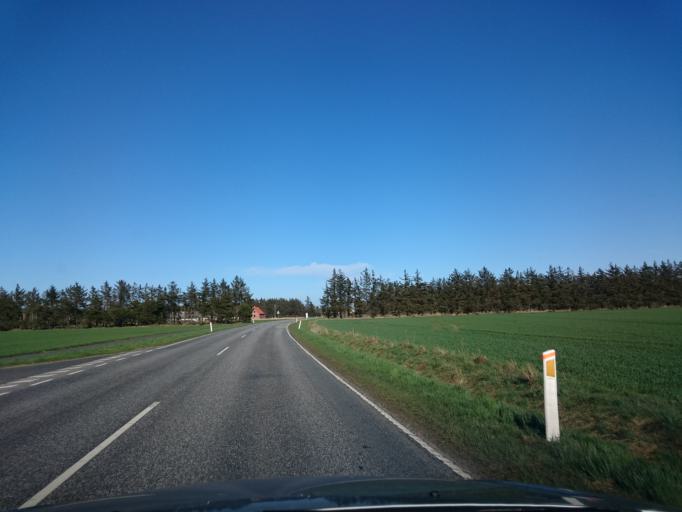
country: DK
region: North Denmark
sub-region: Hjorring Kommune
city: Sindal
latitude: 57.5792
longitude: 10.1725
